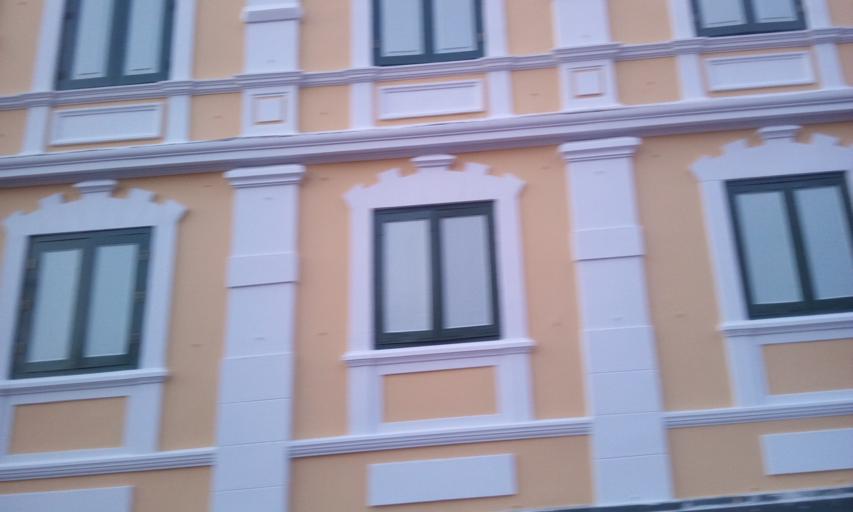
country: TH
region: Bangkok
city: Bangkok
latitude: 13.7511
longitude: 100.4948
